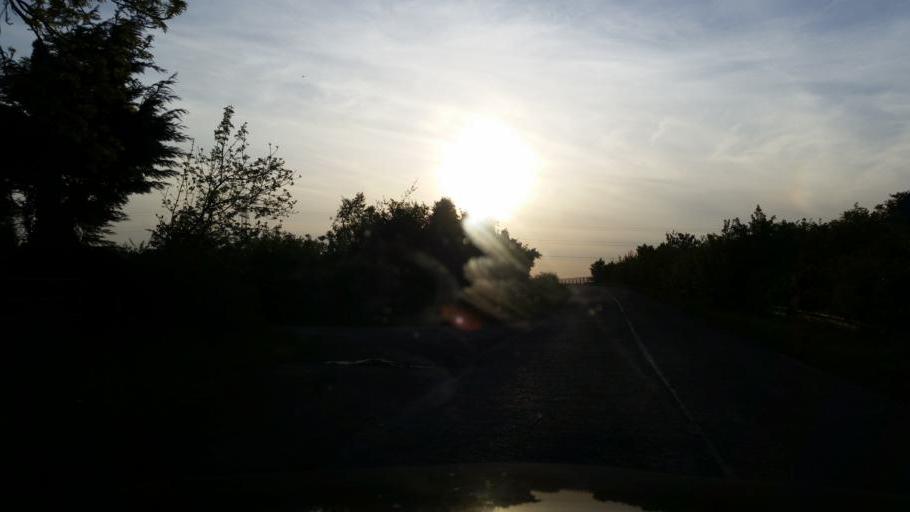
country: IE
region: Leinster
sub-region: Fingal County
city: Swords
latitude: 53.4911
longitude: -6.2013
